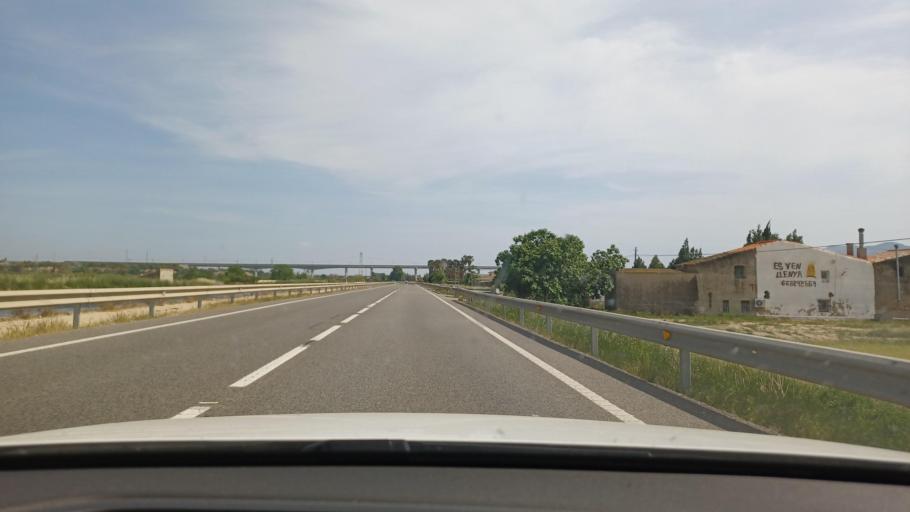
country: ES
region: Catalonia
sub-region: Provincia de Tarragona
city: Amposta
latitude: 40.7394
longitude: 0.5655
